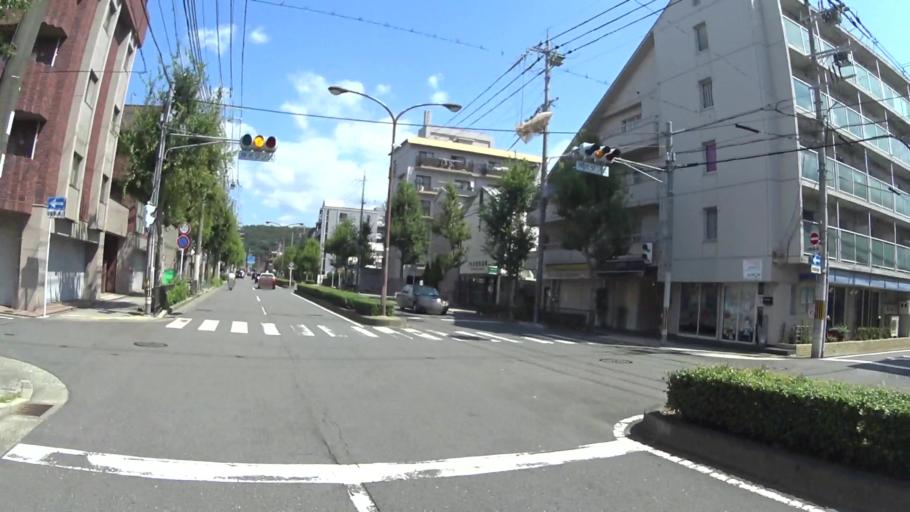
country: JP
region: Kyoto
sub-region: Kyoto-shi
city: Kamigyo-ku
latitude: 35.0488
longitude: 135.7705
